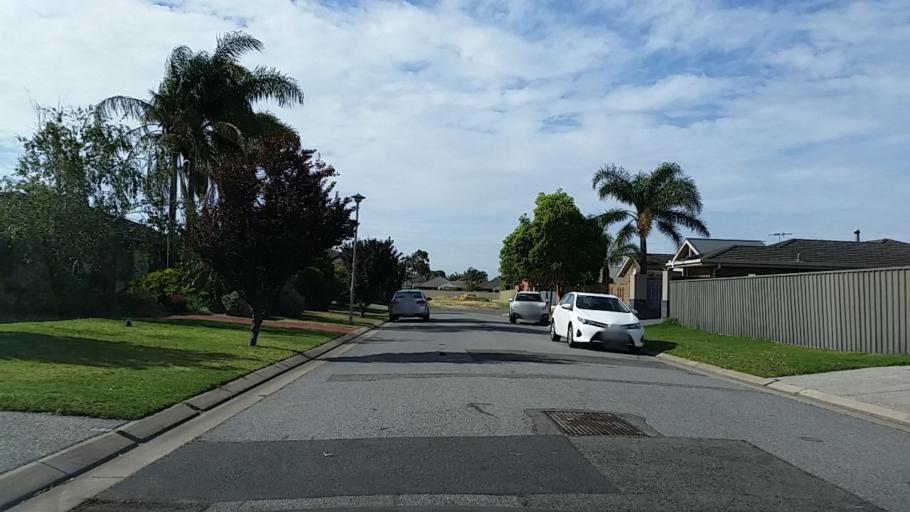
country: AU
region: South Australia
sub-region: Charles Sturt
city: Grange
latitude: -34.8933
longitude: 138.4993
